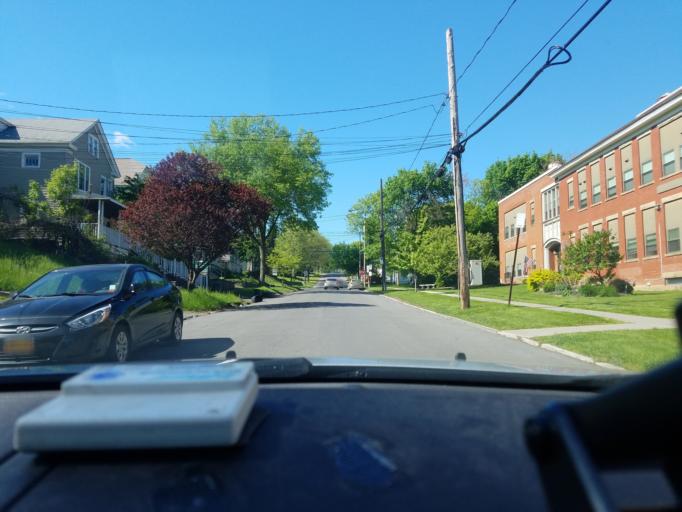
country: US
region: New York
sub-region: Onondaga County
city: Syracuse
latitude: 43.0545
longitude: -76.1235
